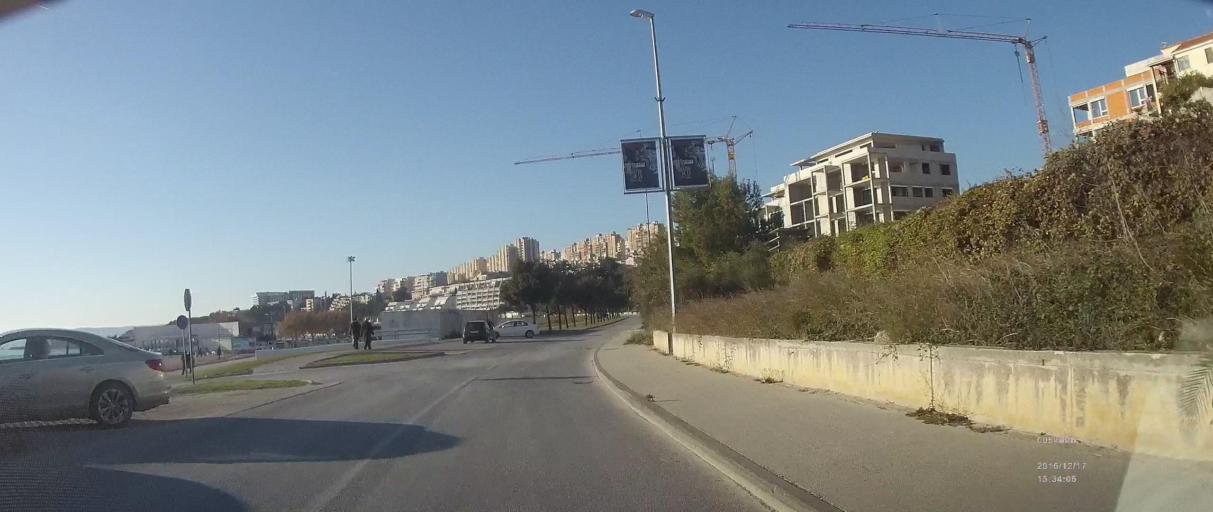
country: HR
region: Splitsko-Dalmatinska
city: Kamen
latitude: 43.5020
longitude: 16.4822
